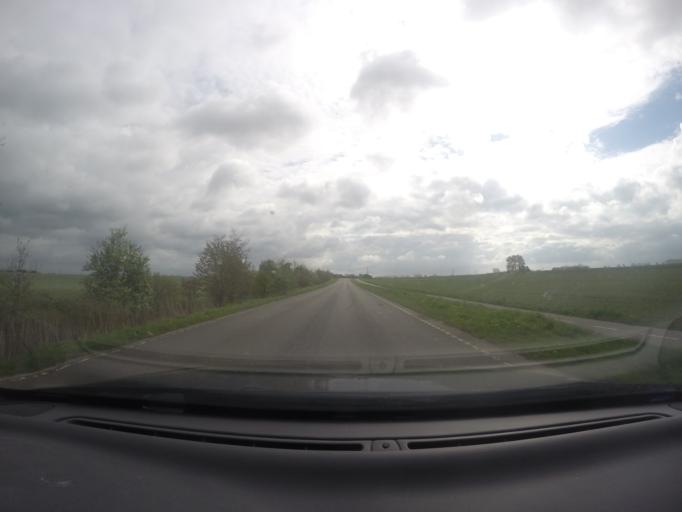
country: DK
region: Capital Region
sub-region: Hoje-Taastrup Kommune
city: Taastrup
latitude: 55.6831
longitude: 12.2712
